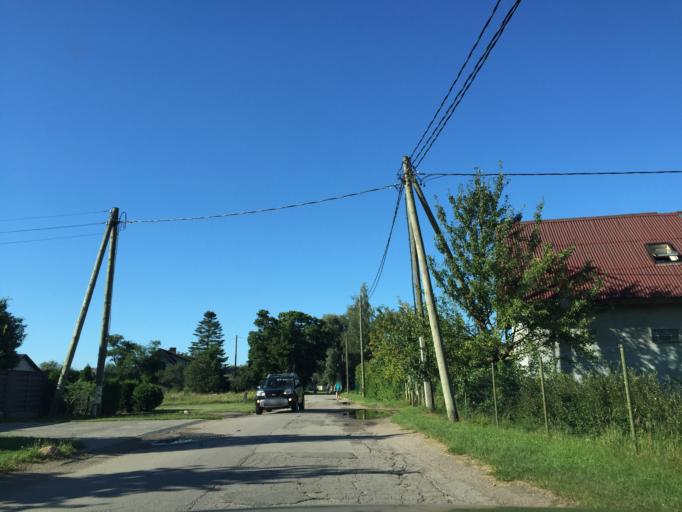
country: LV
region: Riga
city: Jaunciems
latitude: 57.0569
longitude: 24.1383
